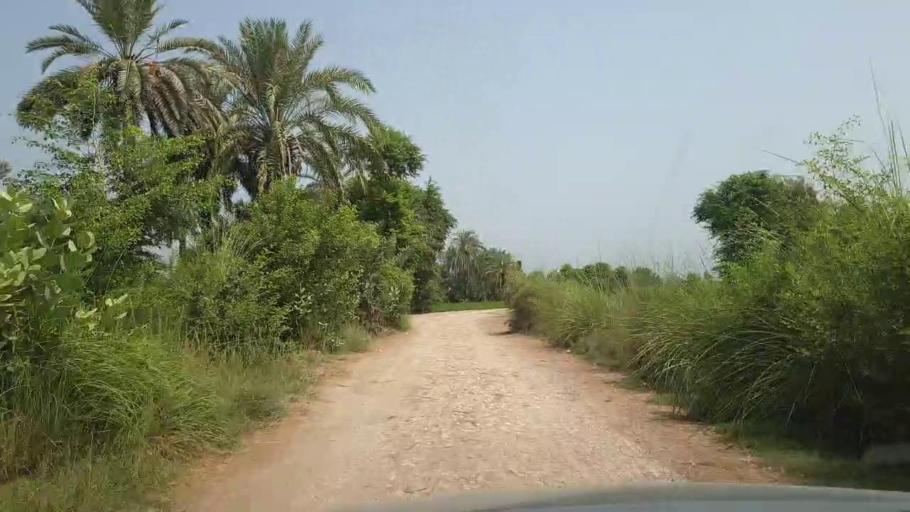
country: PK
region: Sindh
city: Madeji
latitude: 27.7934
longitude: 68.5301
